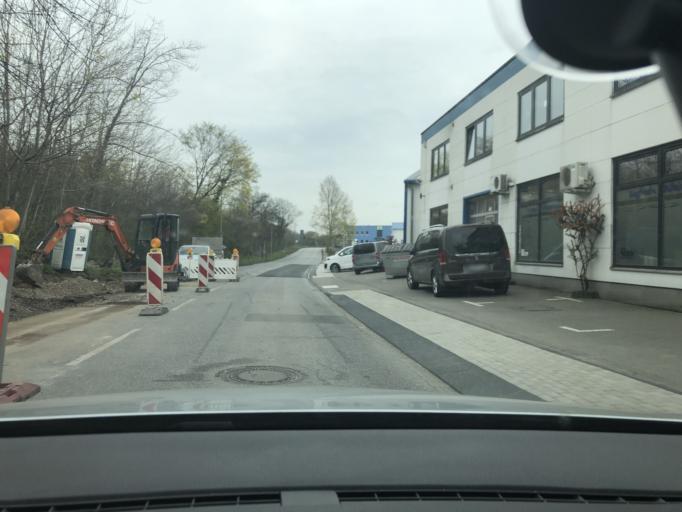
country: DE
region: North Rhine-Westphalia
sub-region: Regierungsbezirk Dusseldorf
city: Duisburg
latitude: 51.4423
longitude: 6.7642
